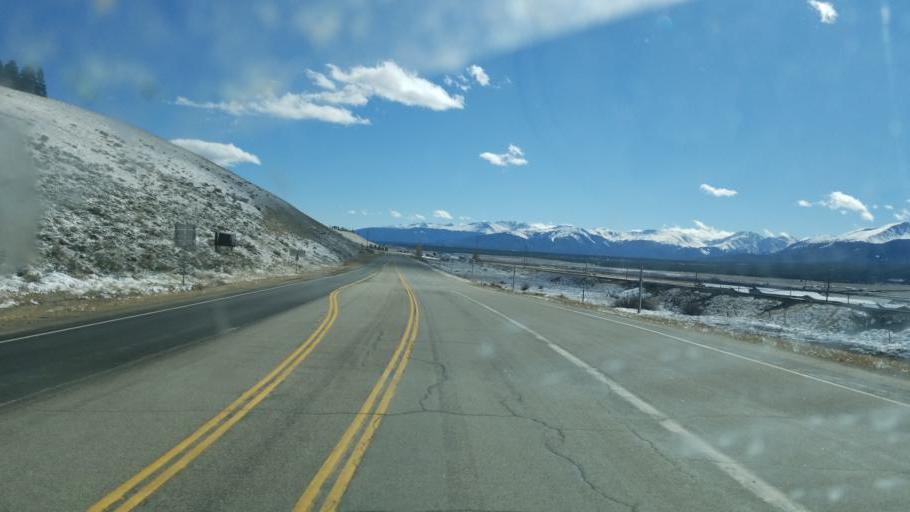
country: US
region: Colorado
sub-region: Lake County
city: Leadville North
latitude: 39.2212
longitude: -106.3487
